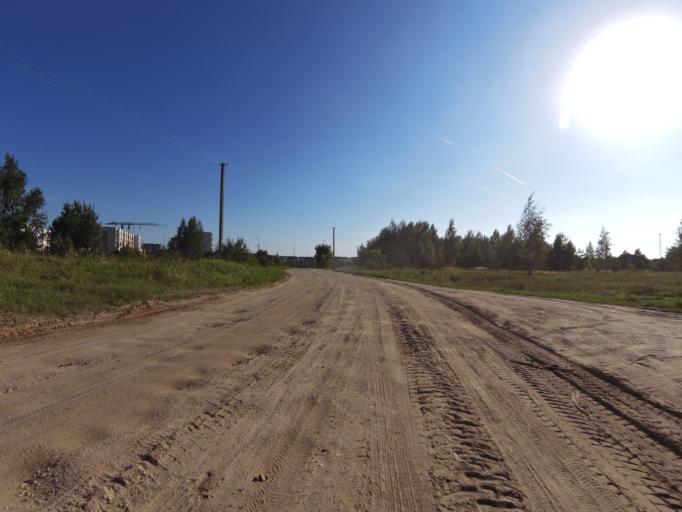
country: LT
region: Vilnius County
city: Pilaite
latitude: 54.7117
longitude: 25.1733
